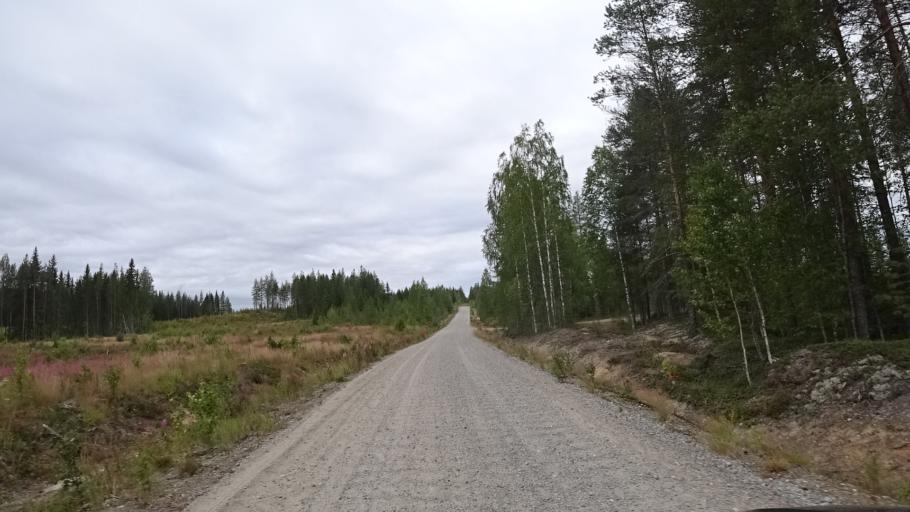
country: FI
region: North Karelia
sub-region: Joensuu
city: Ilomantsi
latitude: 63.1553
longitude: 30.6320
